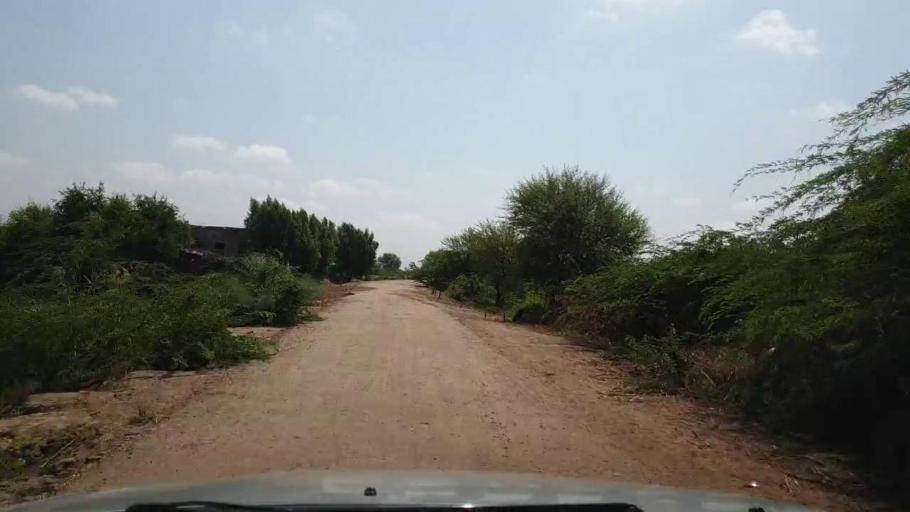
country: PK
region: Sindh
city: Rajo Khanani
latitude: 25.0075
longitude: 68.8581
